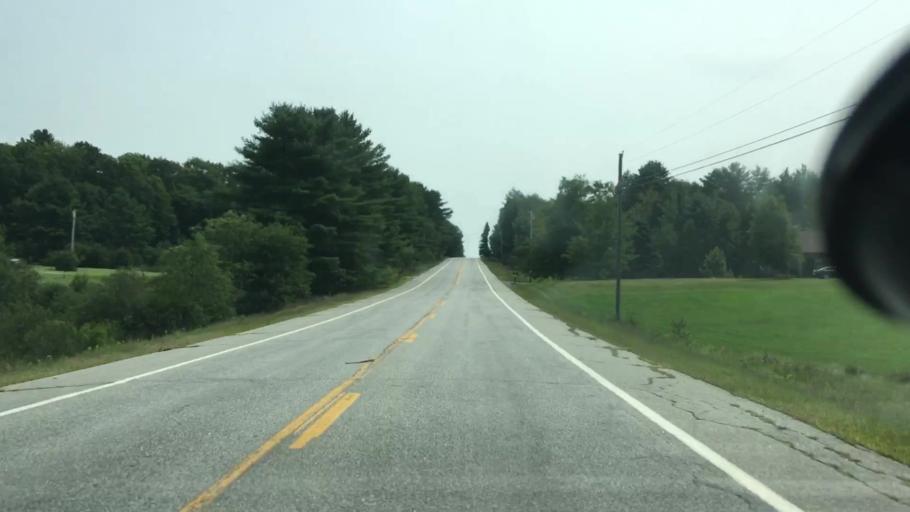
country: US
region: Maine
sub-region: Kennebec County
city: Wayne
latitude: 44.4006
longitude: -70.1252
